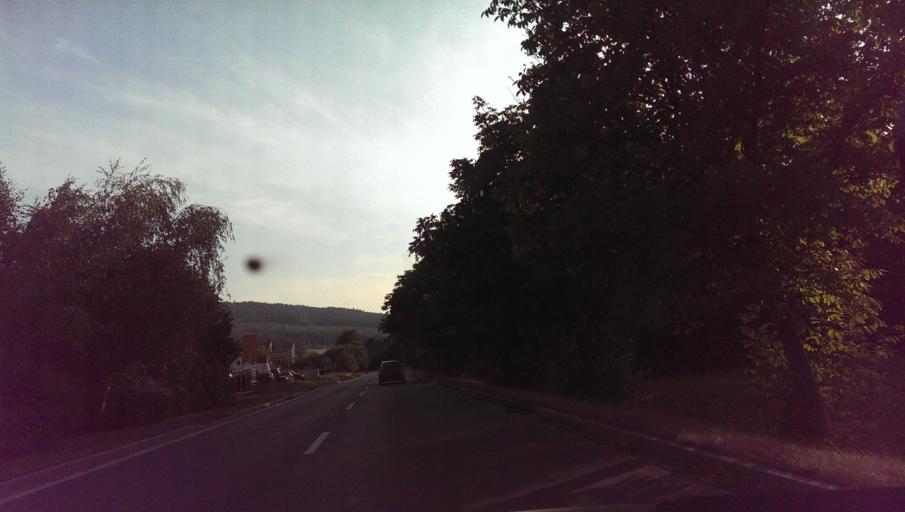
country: CZ
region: Zlin
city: Pozlovice
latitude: 49.1310
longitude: 17.8047
